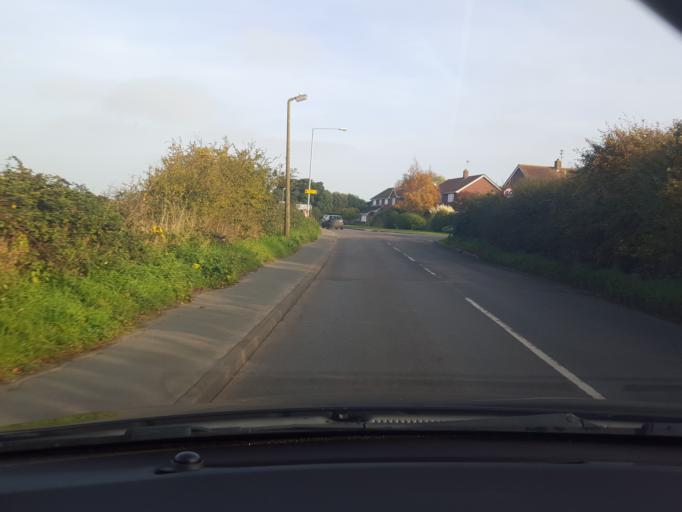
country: GB
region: England
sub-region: Essex
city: Frinton-on-Sea
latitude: 51.8491
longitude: 1.2473
